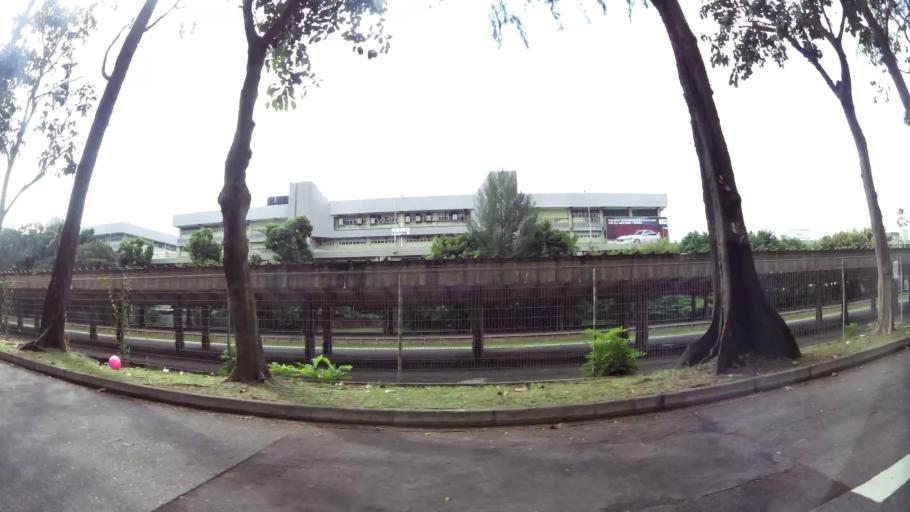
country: SG
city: Singapore
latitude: 1.2732
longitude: 103.8364
